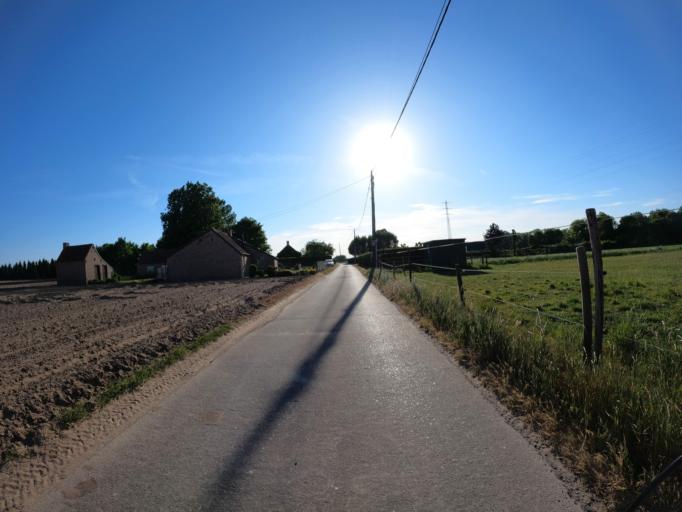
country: BE
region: Flanders
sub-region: Provincie Oost-Vlaanderen
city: Deinze
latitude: 50.9913
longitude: 3.4934
